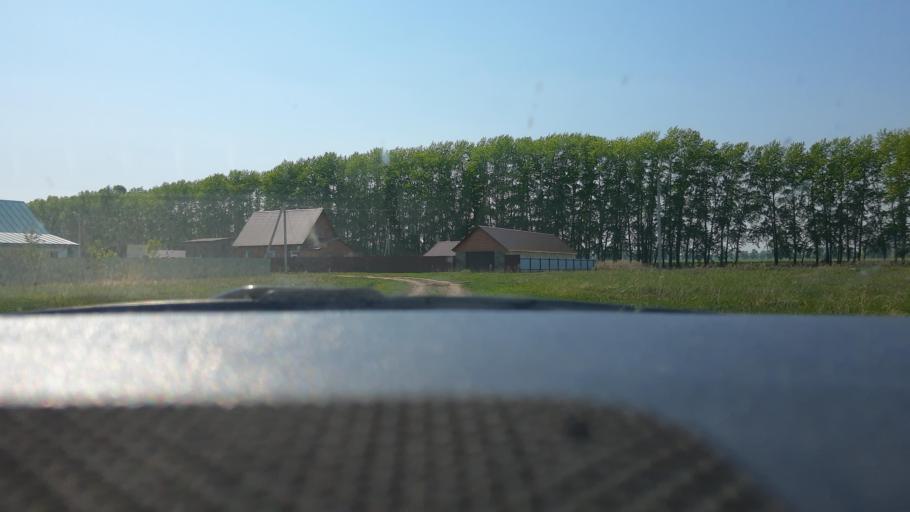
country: RU
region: Bashkortostan
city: Chishmy
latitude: 54.3970
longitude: 55.2117
